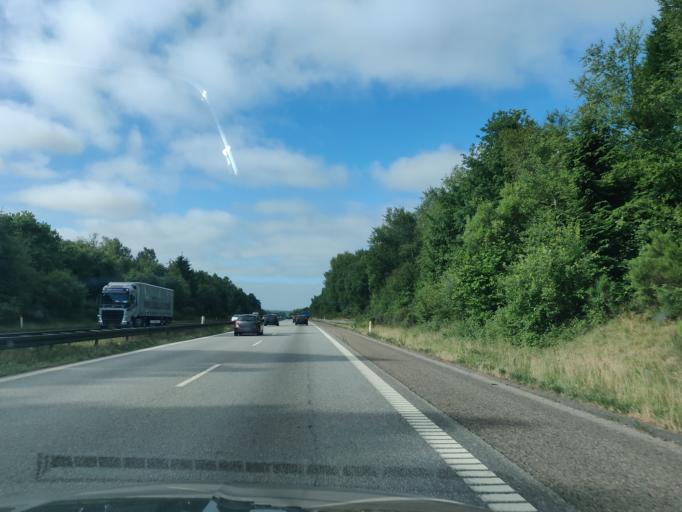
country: DK
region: North Denmark
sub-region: Rebild Kommune
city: Stovring
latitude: 56.9215
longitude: 9.8438
